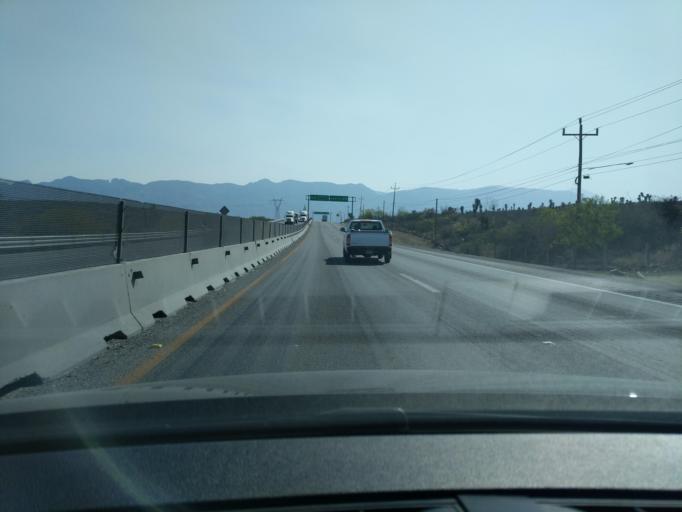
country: MX
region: Nuevo Leon
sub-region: Garcia
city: Los Parques
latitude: 25.7483
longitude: -100.5109
